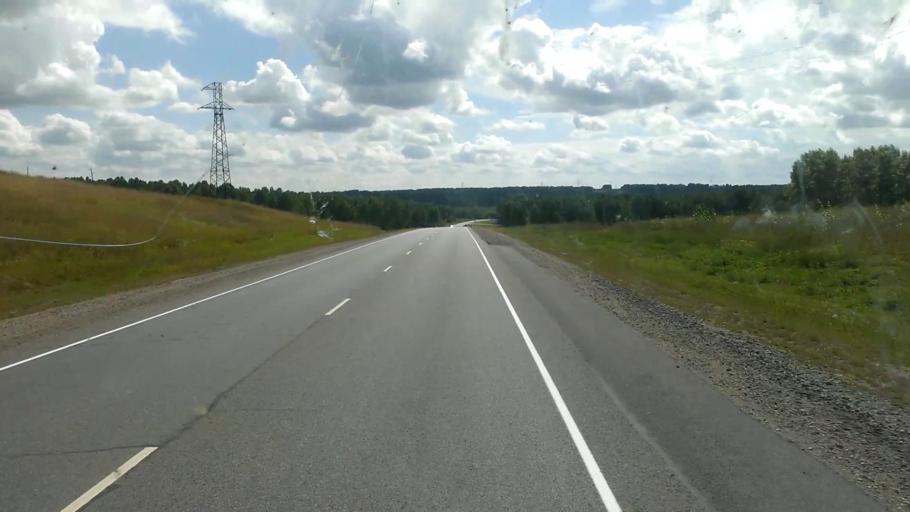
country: RU
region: Altai Krai
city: Troitskoye
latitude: 52.9438
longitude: 84.7764
